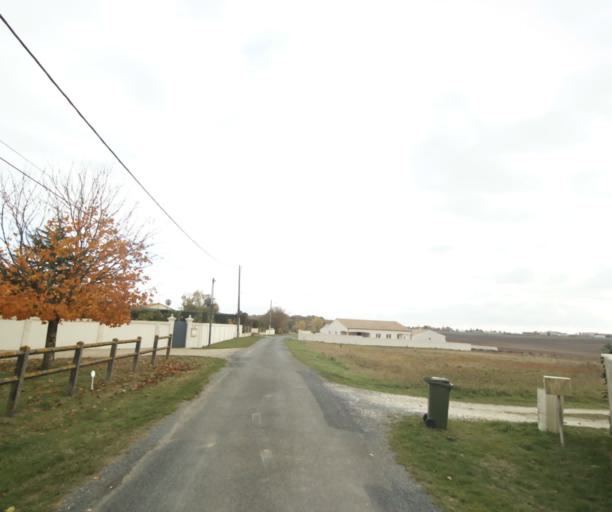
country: FR
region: Poitou-Charentes
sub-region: Departement de la Charente-Maritime
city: Saint-Georges-des-Coteaux
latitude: 45.7797
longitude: -0.7129
